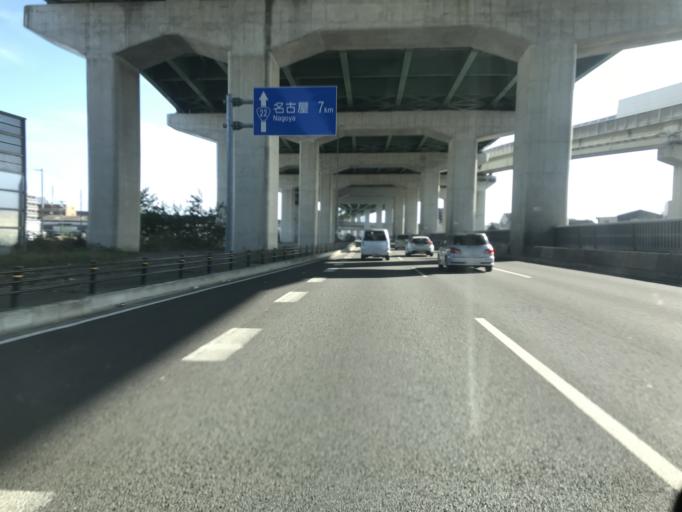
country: JP
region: Aichi
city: Nagoya-shi
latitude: 35.2185
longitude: 136.8564
